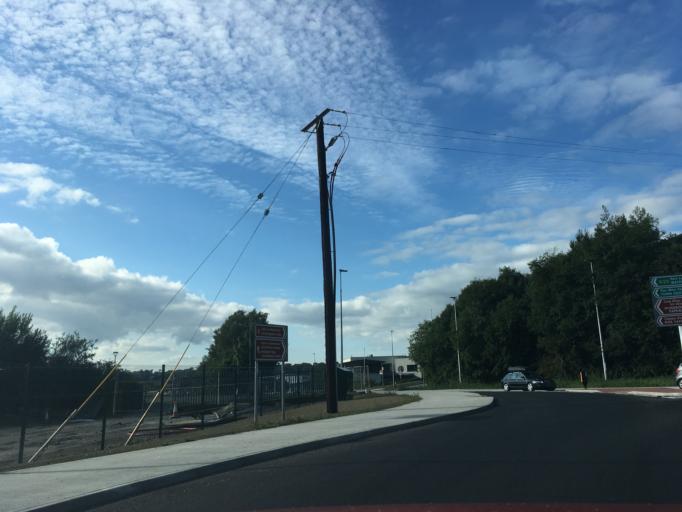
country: IE
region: Leinster
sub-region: Loch Garman
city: New Ross
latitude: 52.3862
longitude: -6.9503
